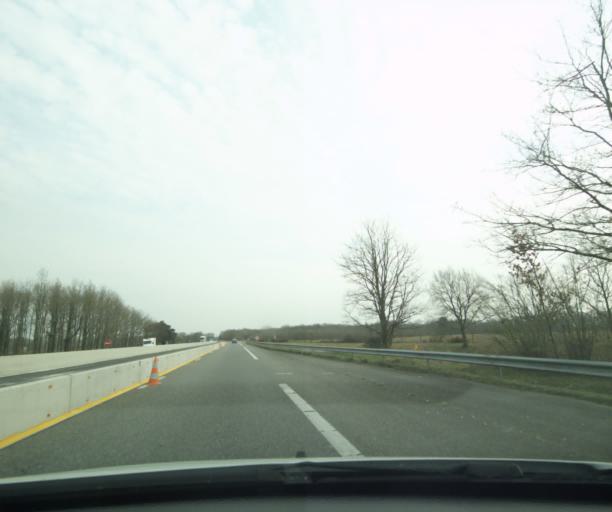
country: FR
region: Aquitaine
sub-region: Departement des Pyrenees-Atlantiques
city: Artix
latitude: 43.3965
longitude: -0.5483
